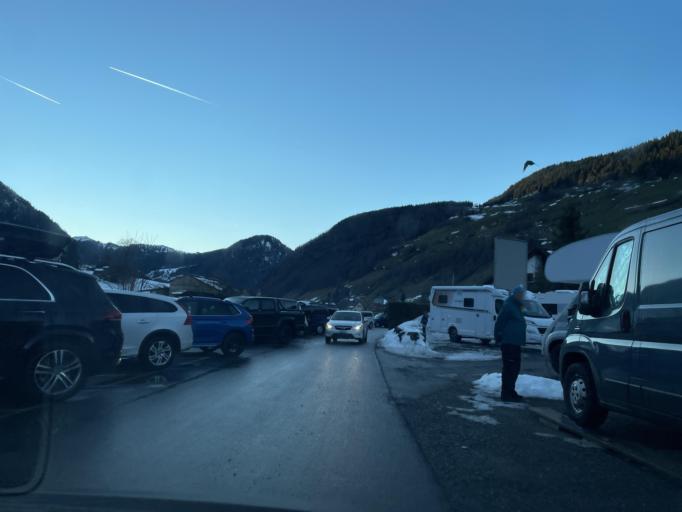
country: CH
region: Saint Gallen
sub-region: Wahlkreis Toggenburg
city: Wildhaus
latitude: 47.1936
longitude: 9.2878
